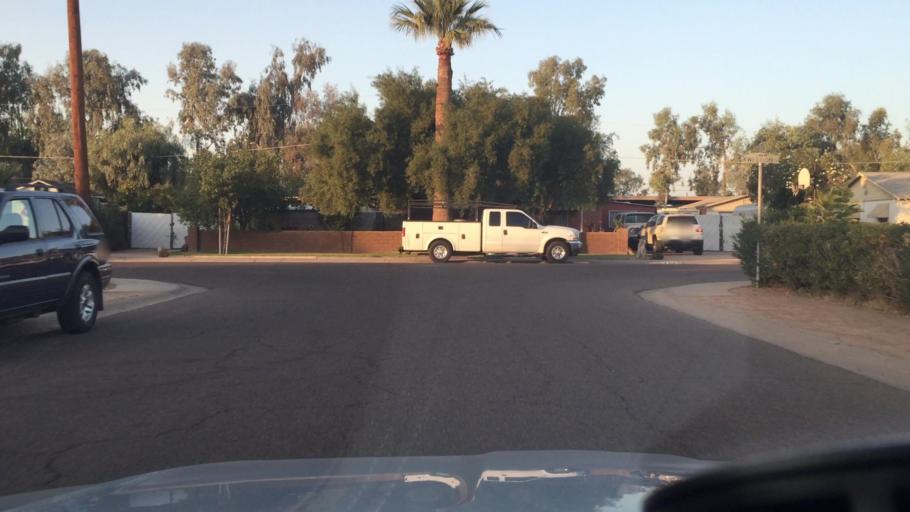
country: US
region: Arizona
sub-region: Maricopa County
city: Phoenix
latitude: 33.4901
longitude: -112.0633
